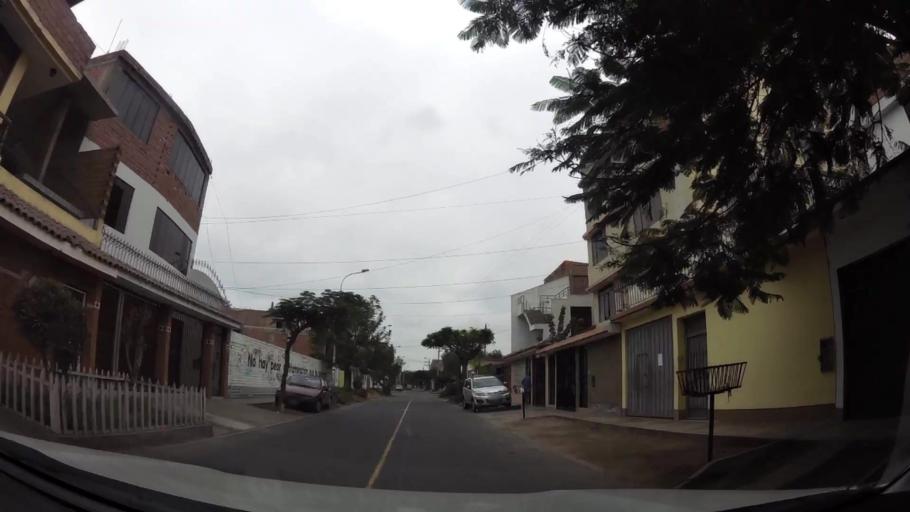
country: PE
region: Lima
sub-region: Lima
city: Surco
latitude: -12.1654
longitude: -76.9914
